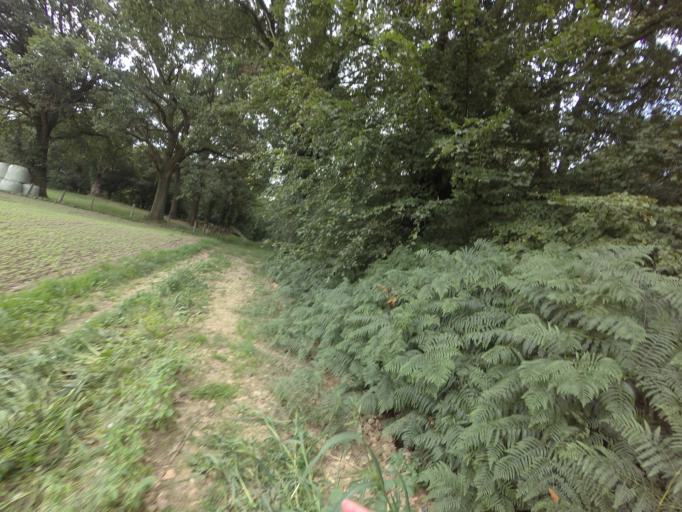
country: NL
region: Limburg
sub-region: Gemeente Simpelveld
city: Simpelveld
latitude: 50.7980
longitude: 5.9894
